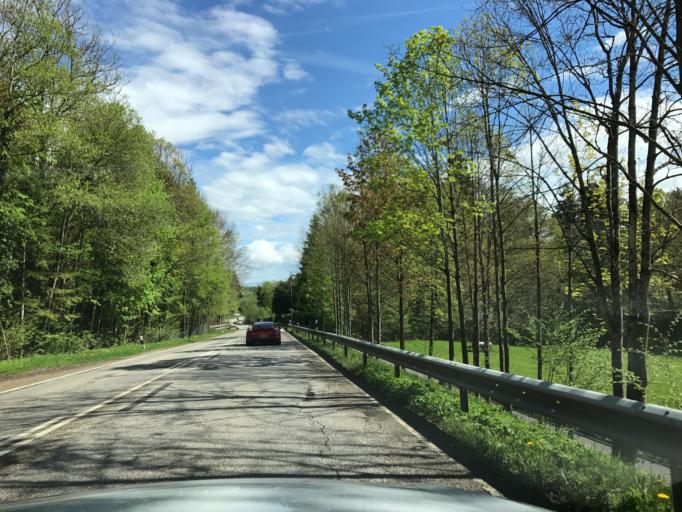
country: DE
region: Bavaria
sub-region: Upper Bavaria
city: Bad Wiessee
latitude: 47.7317
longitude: 11.7170
